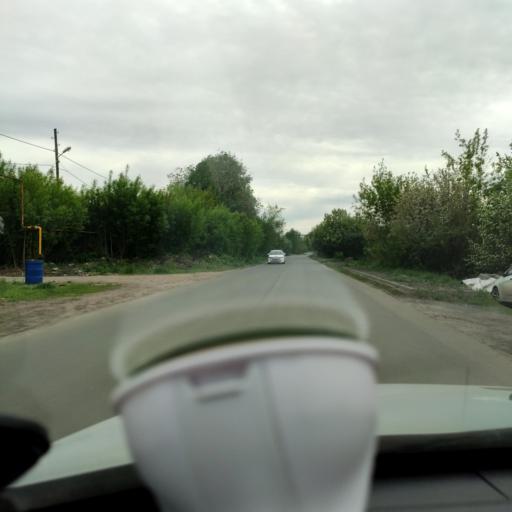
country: RU
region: Samara
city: Smyshlyayevka
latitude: 53.2184
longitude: 50.3341
